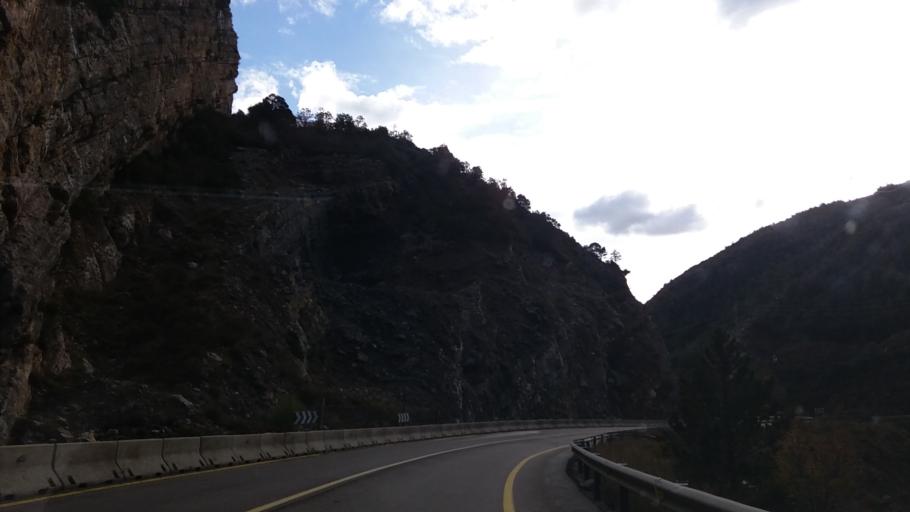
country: ES
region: Aragon
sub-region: Provincia de Huesca
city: Arguis
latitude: 42.2991
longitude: -0.4268
